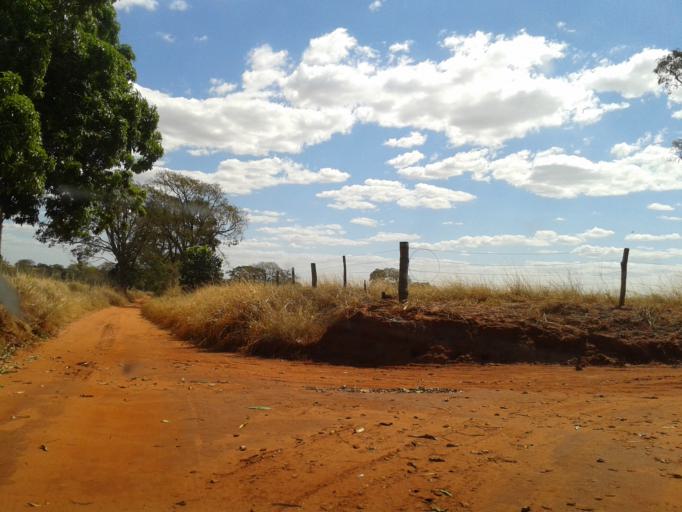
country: BR
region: Minas Gerais
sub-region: Centralina
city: Centralina
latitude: -18.7771
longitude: -49.0903
